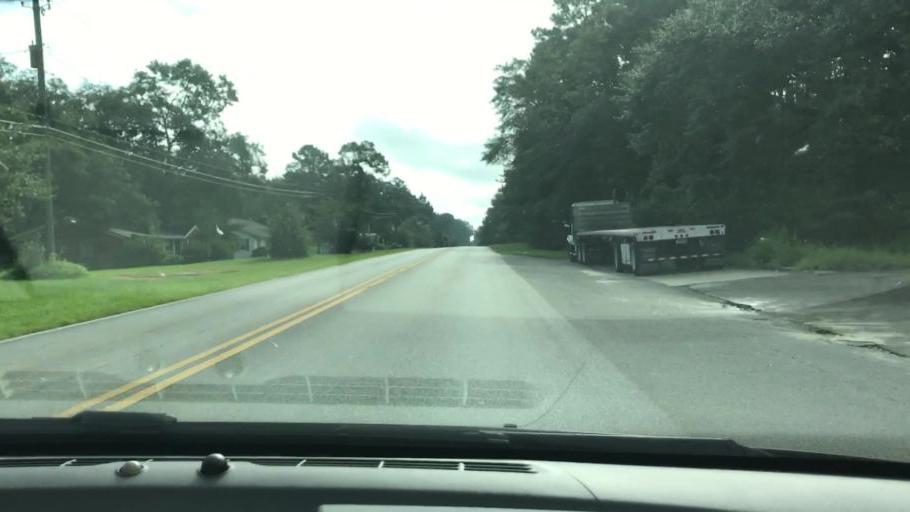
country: US
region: Florida
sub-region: Jackson County
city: Marianna
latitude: 30.7690
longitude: -85.2416
